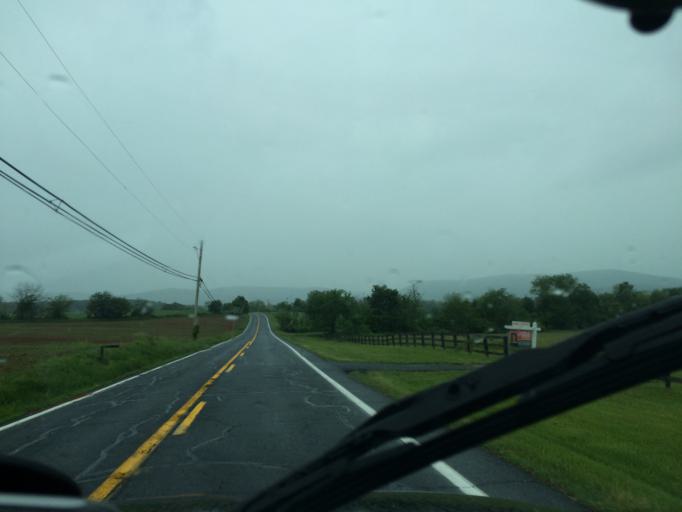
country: US
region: Maryland
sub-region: Frederick County
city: Thurmont
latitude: 39.6158
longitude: -77.3679
